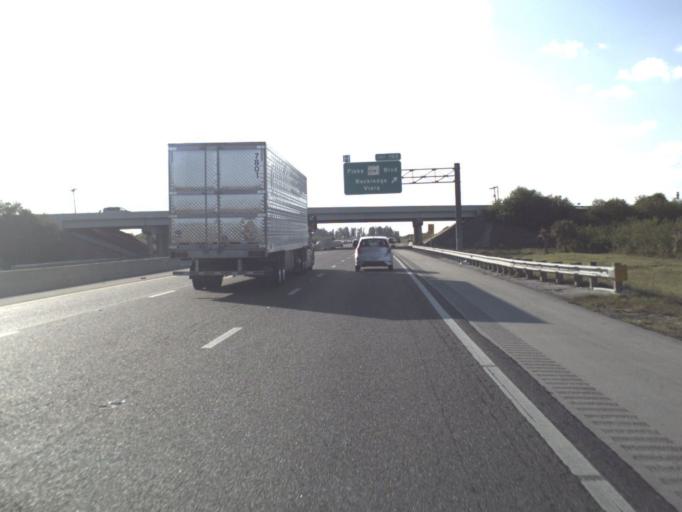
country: US
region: Florida
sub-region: Brevard County
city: Rockledge
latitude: 28.2915
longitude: -80.7413
